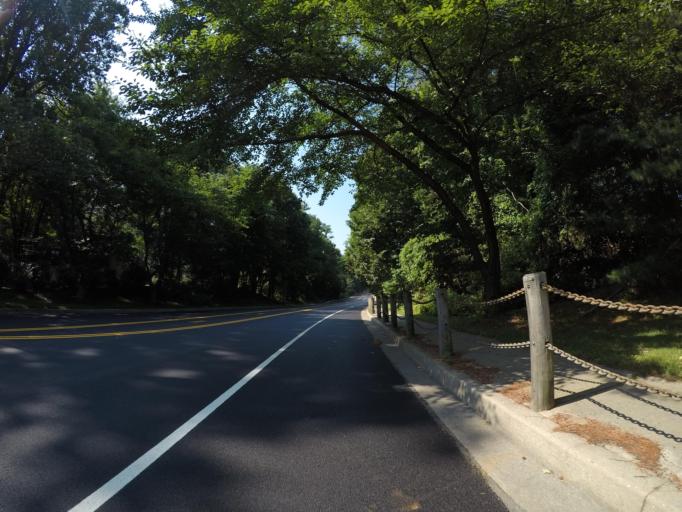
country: US
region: Maryland
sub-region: Howard County
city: Columbia
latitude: 39.2641
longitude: -76.8621
